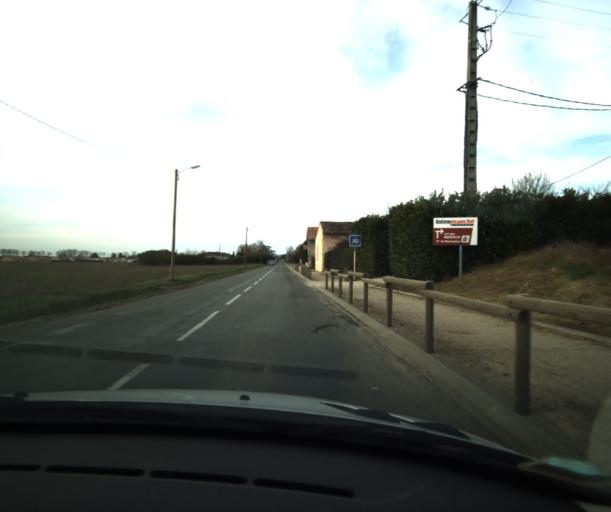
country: FR
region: Midi-Pyrenees
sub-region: Departement du Tarn-et-Garonne
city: Montech
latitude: 43.9495
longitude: 1.2334
